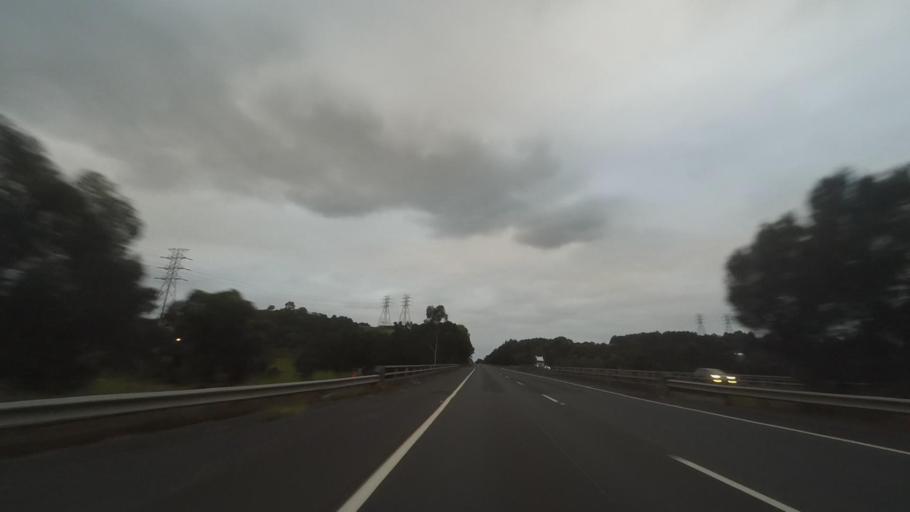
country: AU
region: New South Wales
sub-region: Wollongong
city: Berkeley
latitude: -34.4740
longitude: 150.8314
